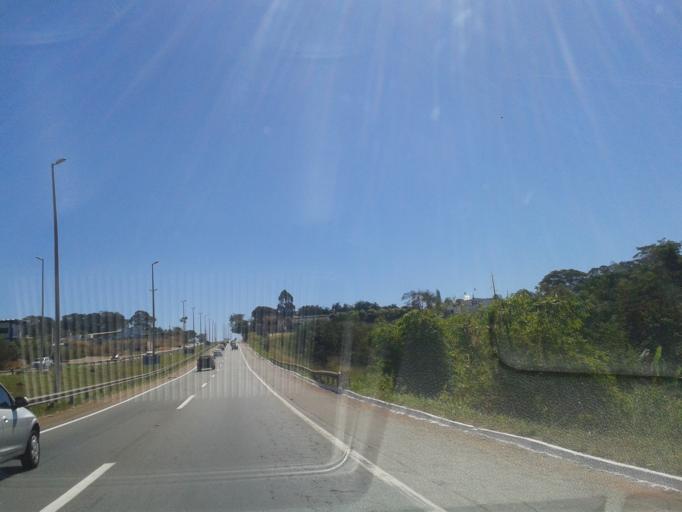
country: BR
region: Goias
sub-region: Goiania
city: Goiania
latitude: -16.6339
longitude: -49.3466
